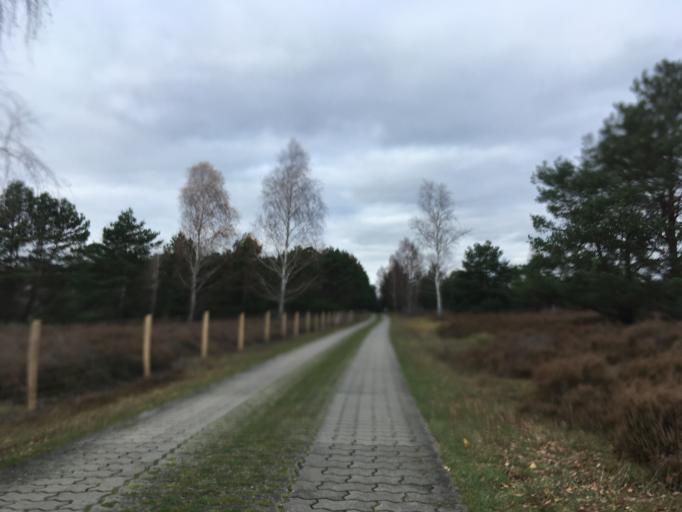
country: DE
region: Brandenburg
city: Tauer
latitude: 52.0133
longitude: 14.4897
